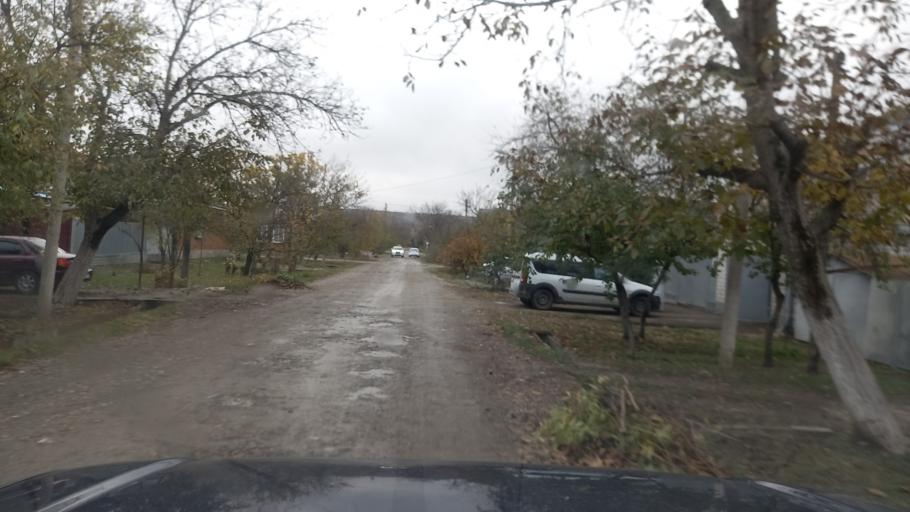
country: RU
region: Adygeya
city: Maykop
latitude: 44.6043
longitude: 40.0850
